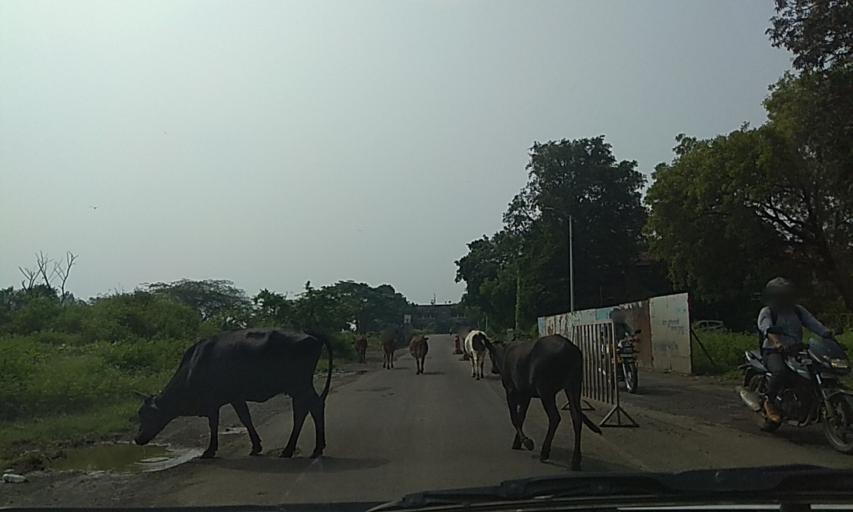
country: IN
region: Maharashtra
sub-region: Pune Division
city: Shivaji Nagar
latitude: 18.5465
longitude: 73.8471
